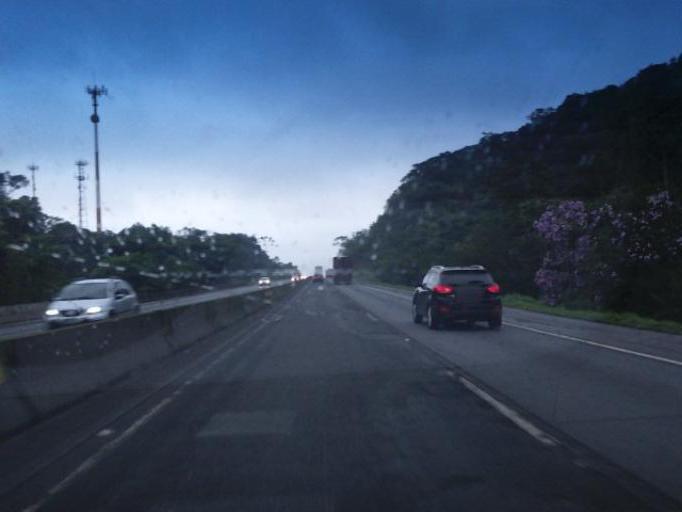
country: BR
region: Santa Catarina
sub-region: Joinville
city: Joinville
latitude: -26.0837
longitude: -48.8619
